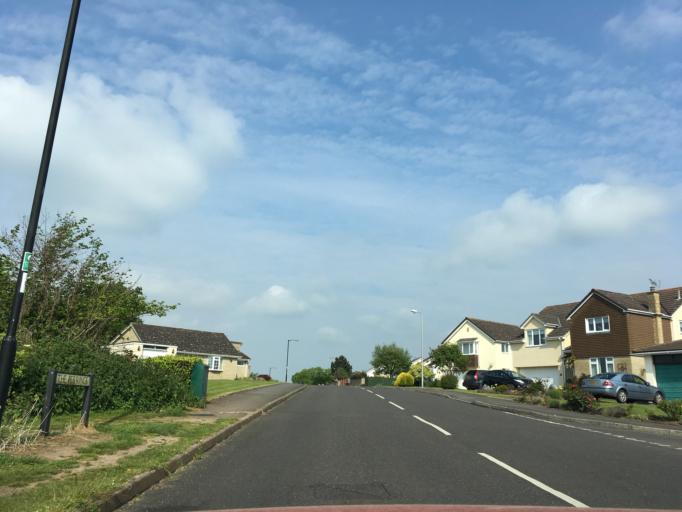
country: GB
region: England
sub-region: North Somerset
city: Nailsea
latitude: 51.4242
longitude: -2.7585
